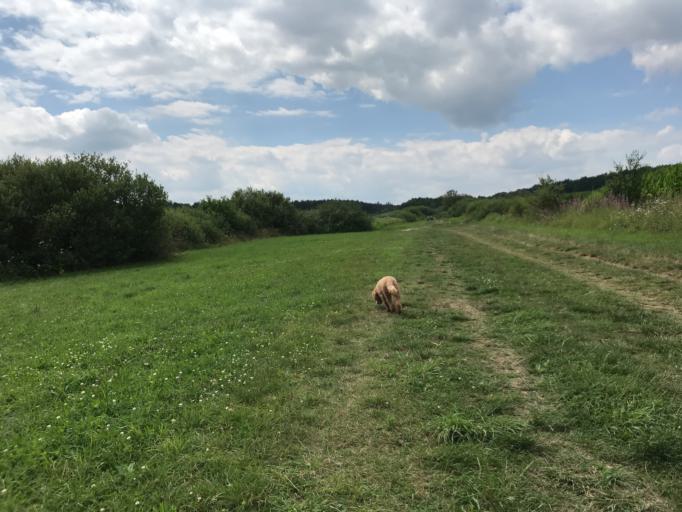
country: CZ
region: Jihocesky
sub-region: Okres Jindrichuv Hradec
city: Trebon
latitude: 48.9931
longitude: 14.7356
